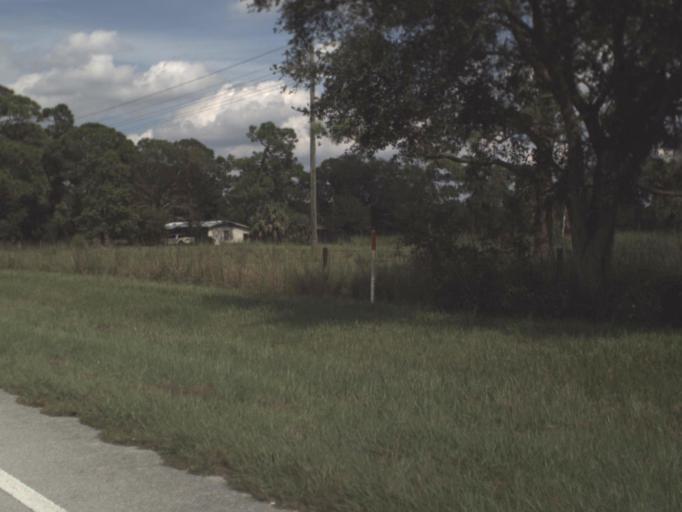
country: US
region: Florida
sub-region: Okeechobee County
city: Cypress Quarters
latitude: 27.3228
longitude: -80.8245
